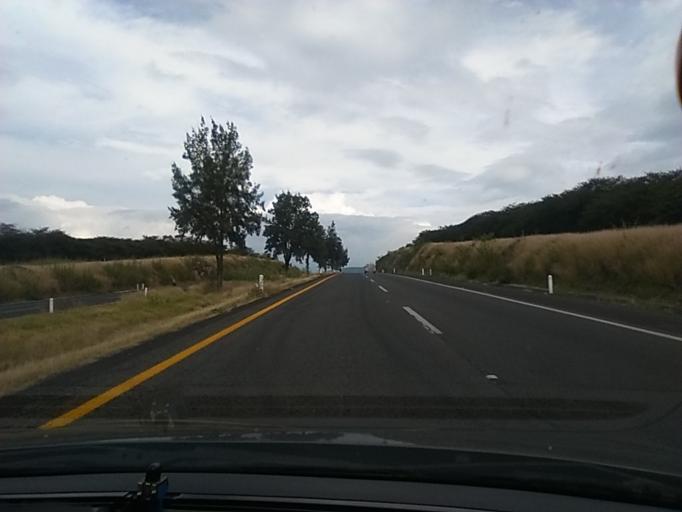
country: MX
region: Michoacan
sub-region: Vista Hermosa
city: La Angostura
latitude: 20.2380
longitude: -102.3939
